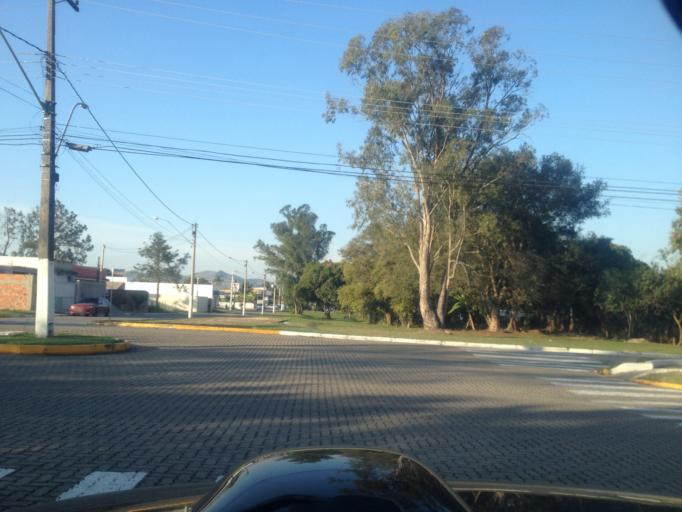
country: BR
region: Rio de Janeiro
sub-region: Porto Real
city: Porto Real
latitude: -22.4217
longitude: -44.2917
